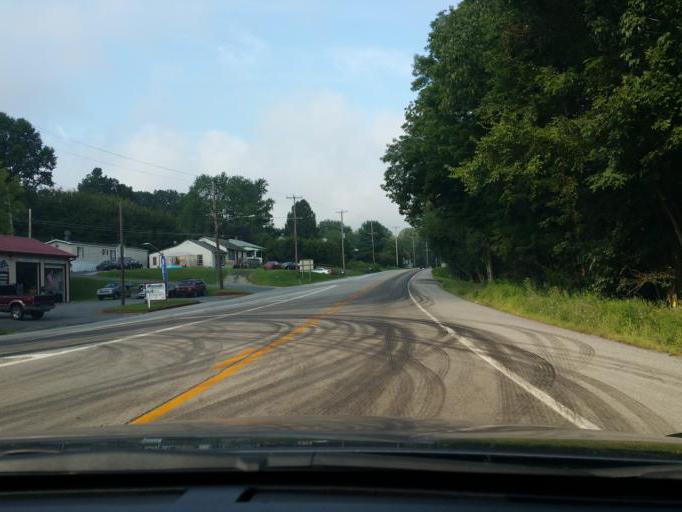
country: US
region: Maryland
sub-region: Cecil County
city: Rising Sun
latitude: 39.6949
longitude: -76.0943
